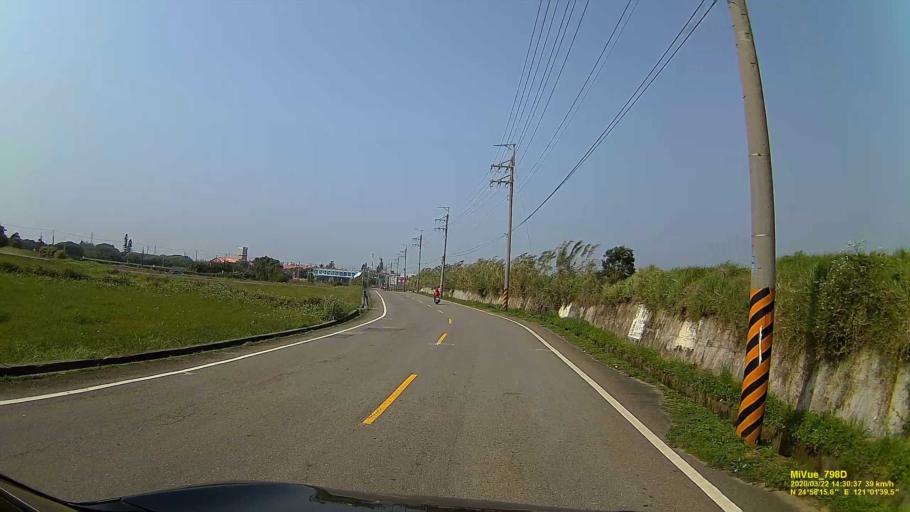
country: TW
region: Taiwan
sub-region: Hsinchu
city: Zhubei
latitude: 24.9713
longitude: 121.0277
